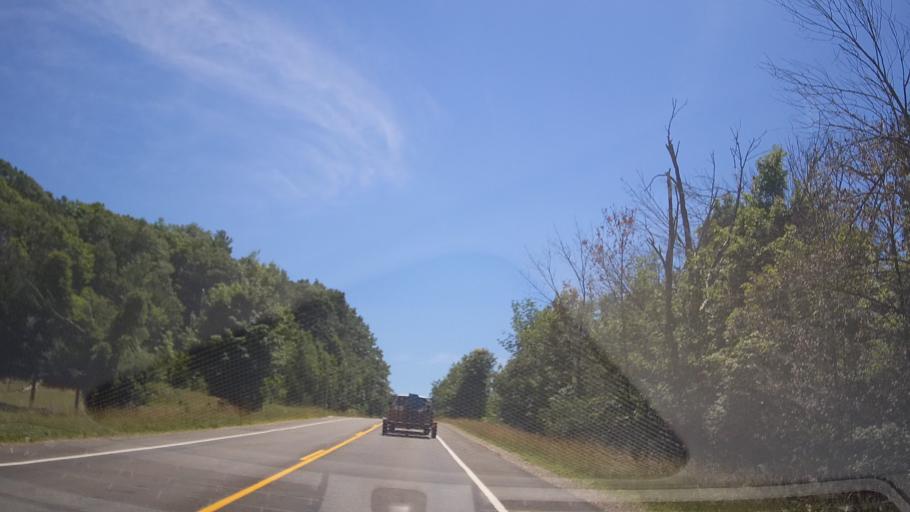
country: US
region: Michigan
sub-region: Grand Traverse County
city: Traverse City
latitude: 44.6258
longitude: -85.6965
